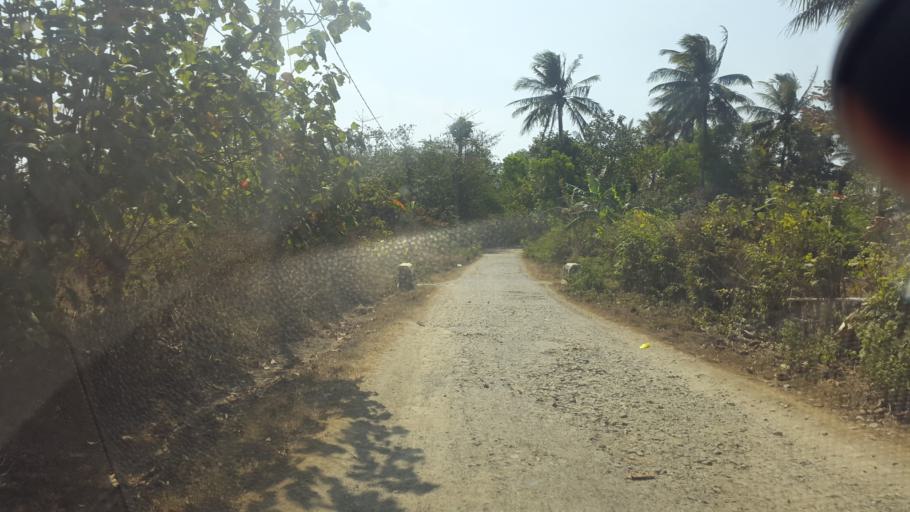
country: ID
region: West Java
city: Gunungbatu
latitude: -7.3417
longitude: 106.4018
